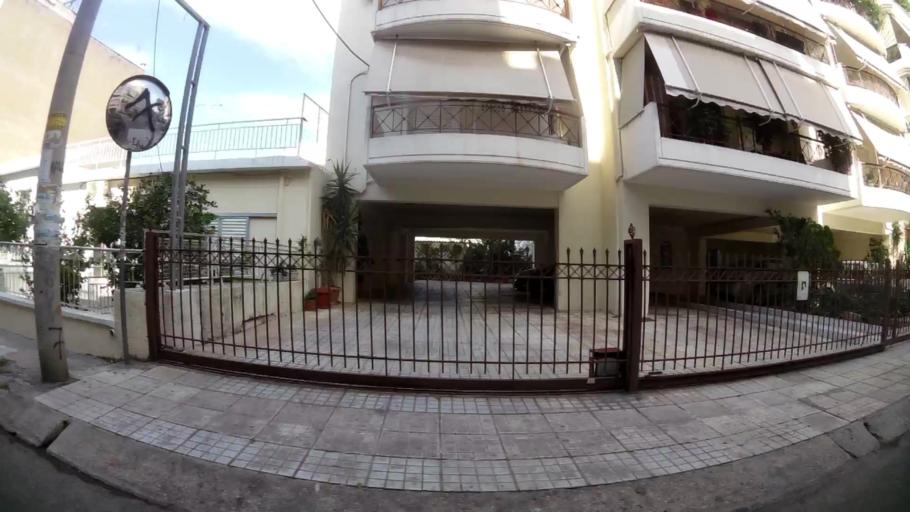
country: GR
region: Attica
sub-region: Nomos Piraios
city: Keratsini
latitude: 37.9623
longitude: 23.6177
